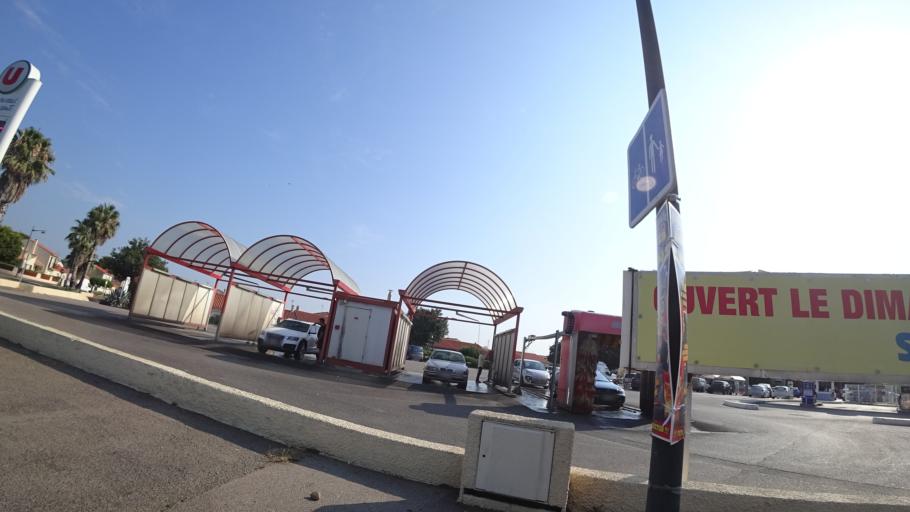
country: FR
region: Languedoc-Roussillon
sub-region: Departement des Pyrenees-Orientales
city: Bompas
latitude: 42.7214
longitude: 2.9325
